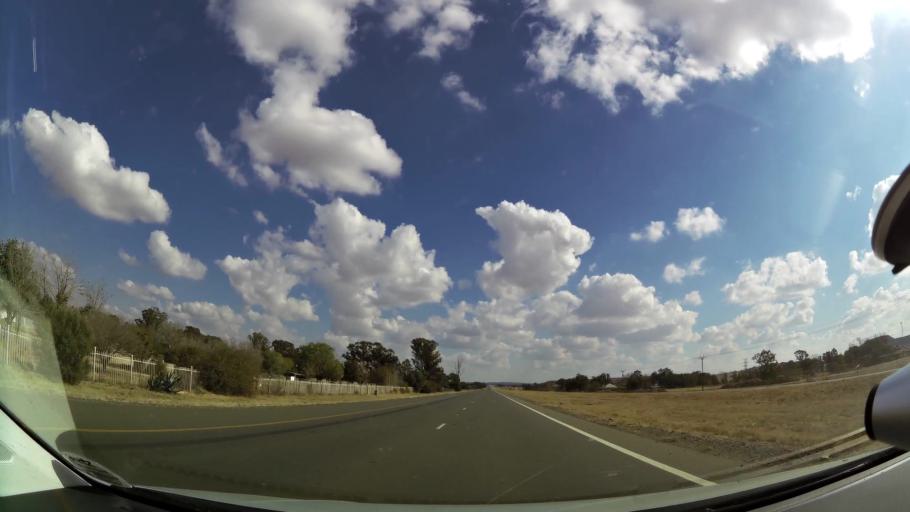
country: ZA
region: Orange Free State
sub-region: Mangaung Metropolitan Municipality
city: Bloemfontein
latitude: -29.1333
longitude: 26.1411
